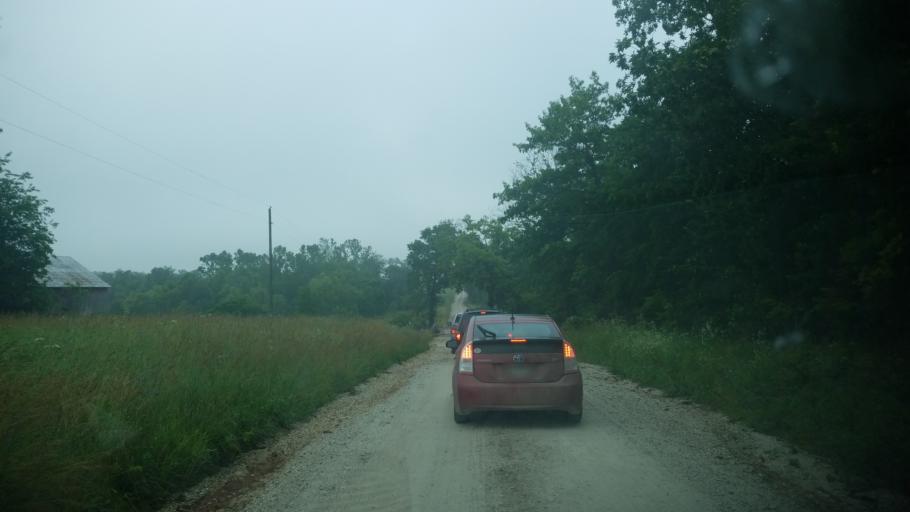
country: US
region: Missouri
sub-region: Pike County
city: Bowling Green
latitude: 39.3078
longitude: -91.2889
